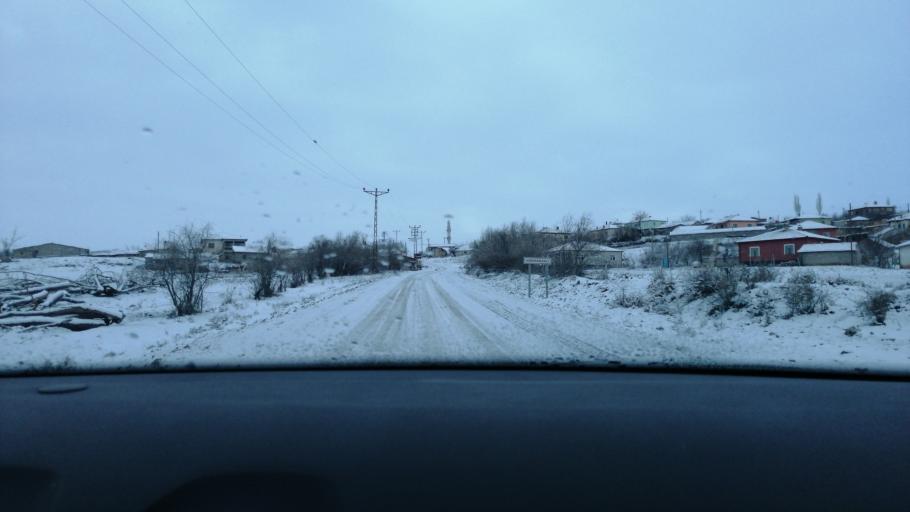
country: TR
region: Aksaray
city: Agacoren
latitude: 38.9371
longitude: 33.9483
